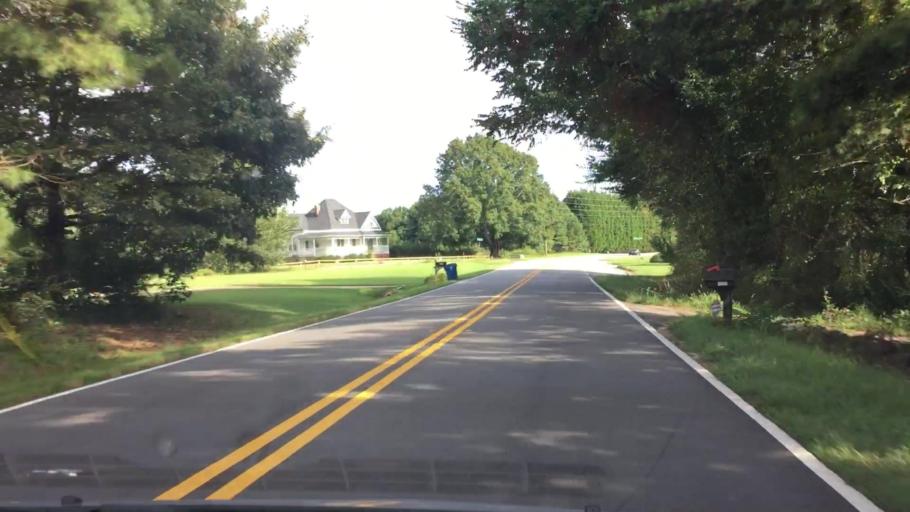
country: US
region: Georgia
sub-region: Clayton County
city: Conley
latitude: 33.6389
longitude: -84.2603
